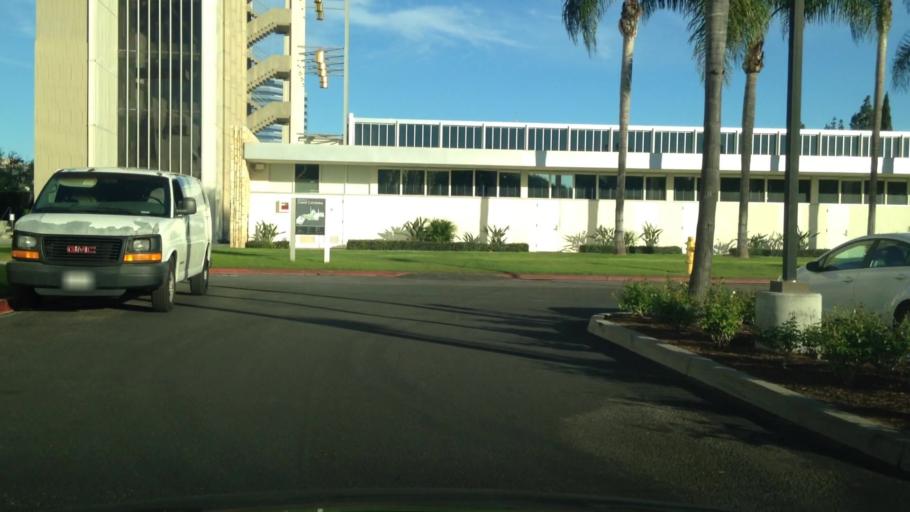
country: US
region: California
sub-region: Orange County
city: Garden Grove
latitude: 33.7867
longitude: -117.9000
